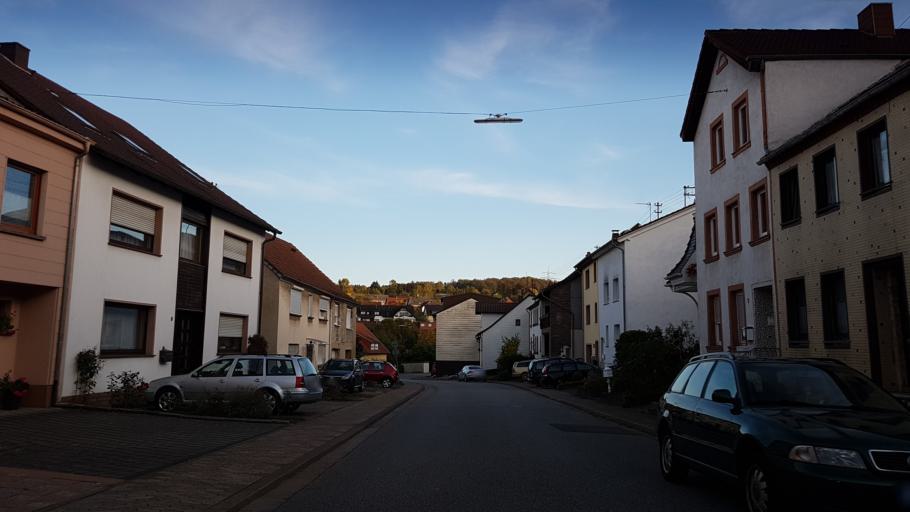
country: DE
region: Saarland
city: Eppelborn
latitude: 49.4034
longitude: 6.9672
